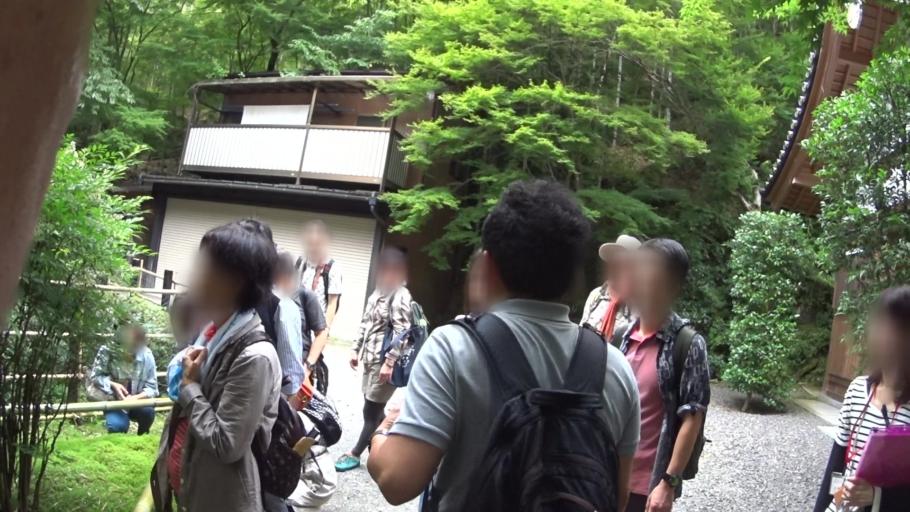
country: JP
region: Kyoto
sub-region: Kyoto-shi
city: Kamigyo-ku
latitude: 35.0573
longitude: 135.6743
